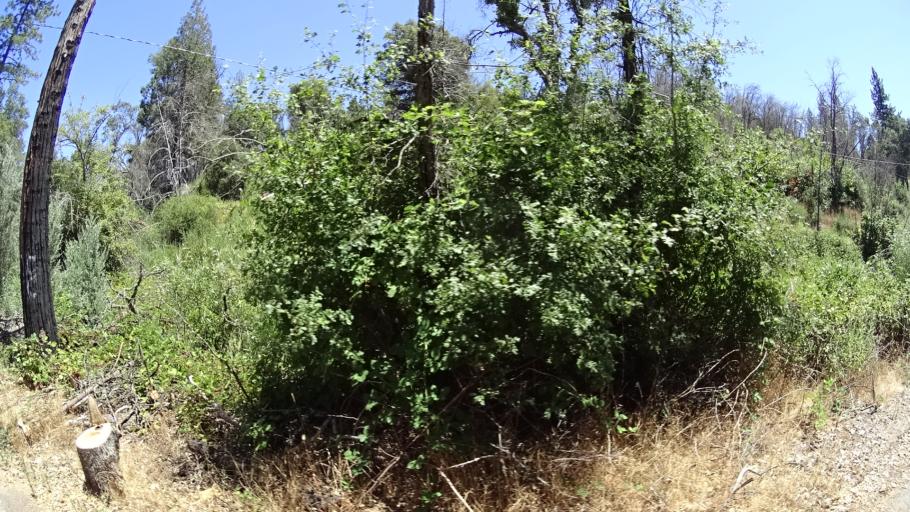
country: US
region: California
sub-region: Calaveras County
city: Mountain Ranch
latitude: 38.2426
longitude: -120.5454
